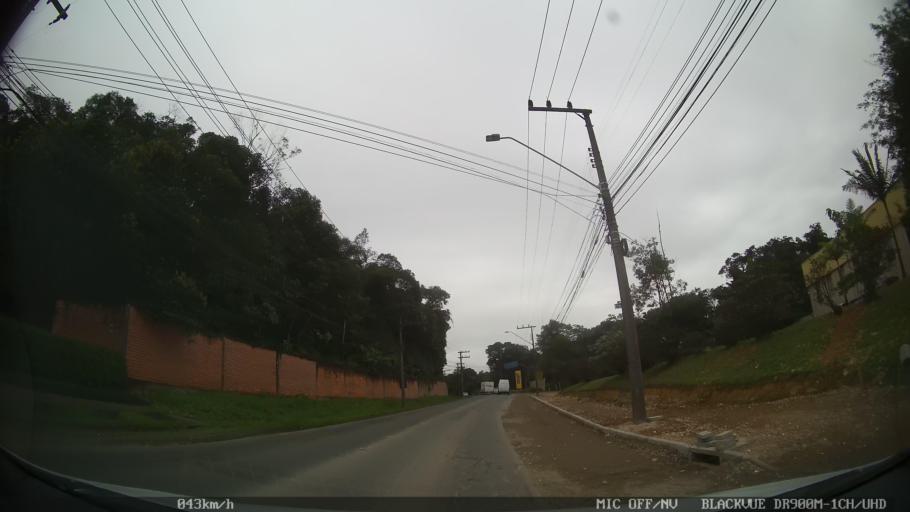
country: BR
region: Santa Catarina
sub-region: Joinville
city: Joinville
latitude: -26.2484
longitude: -48.8772
